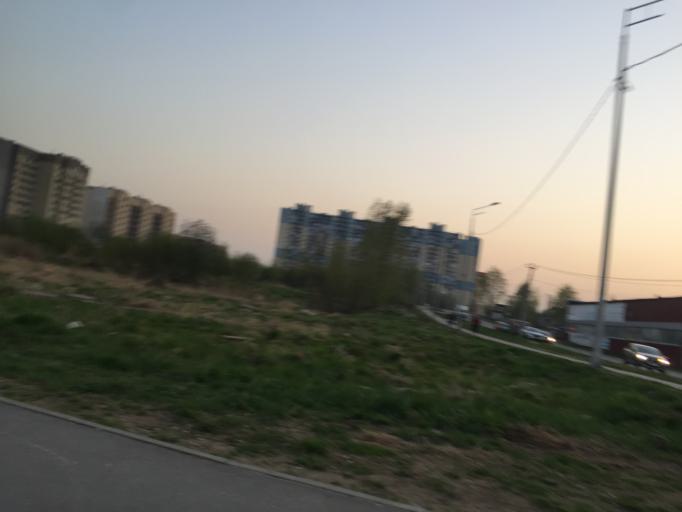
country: RU
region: Leningrad
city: Bugry
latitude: 60.0692
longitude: 30.4075
